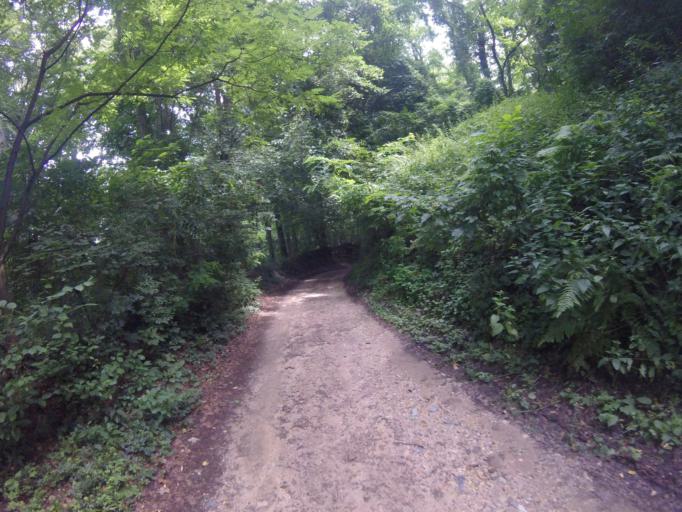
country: HU
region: Zala
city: Lenti
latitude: 46.5735
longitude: 16.6045
